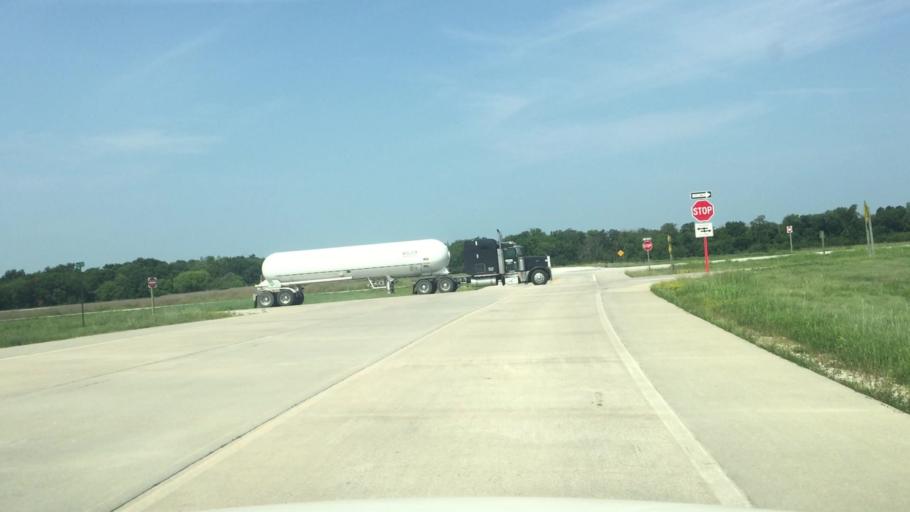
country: US
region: Kansas
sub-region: Montgomery County
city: Coffeyville
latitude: 37.1079
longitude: -95.5856
